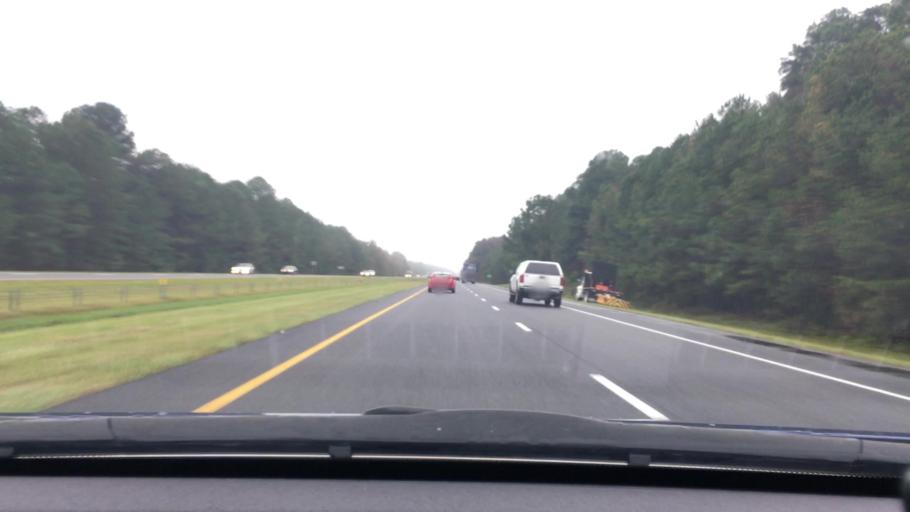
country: US
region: South Carolina
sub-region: Lee County
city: Bishopville
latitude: 34.1976
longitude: -80.1021
